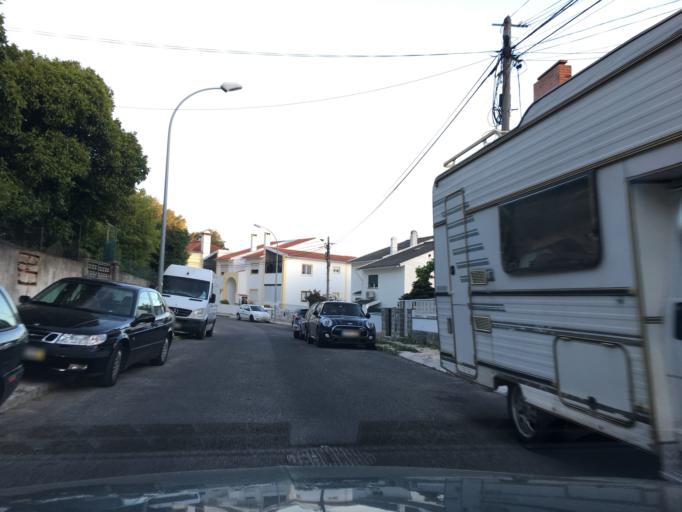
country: PT
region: Lisbon
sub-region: Oeiras
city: Barcarena
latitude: 38.7275
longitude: -9.2770
